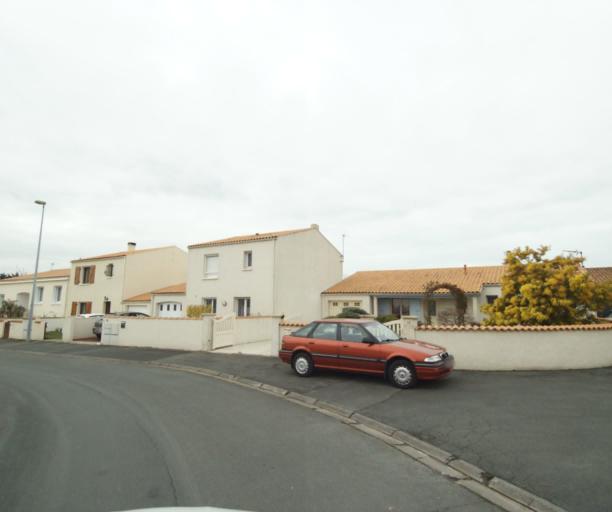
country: FR
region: Poitou-Charentes
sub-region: Departement de la Charente-Maritime
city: Lagord
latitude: 46.1887
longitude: -1.1505
